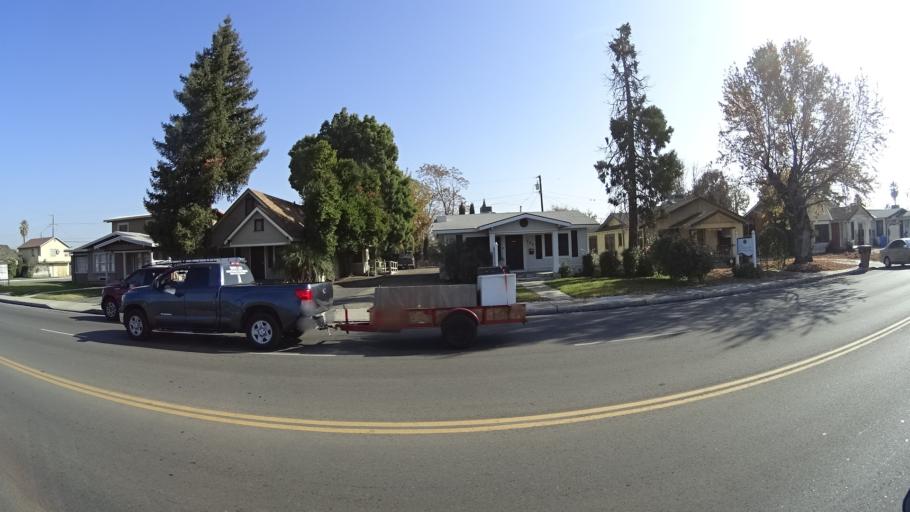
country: US
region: California
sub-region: Kern County
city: Bakersfield
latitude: 35.3566
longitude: -119.0214
